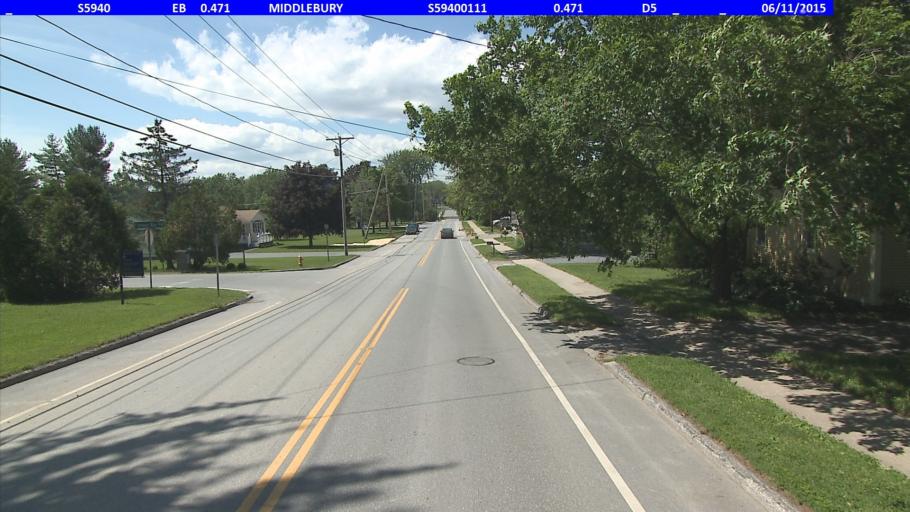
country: US
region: Vermont
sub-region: Addison County
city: Middlebury (village)
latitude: 44.0164
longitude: -73.1777
